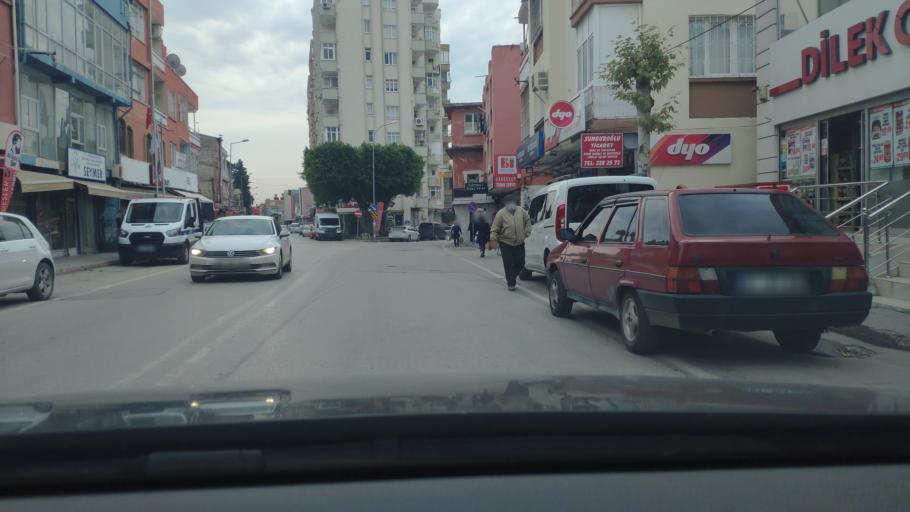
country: TR
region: Adana
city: Adana
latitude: 37.0193
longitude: 35.3141
